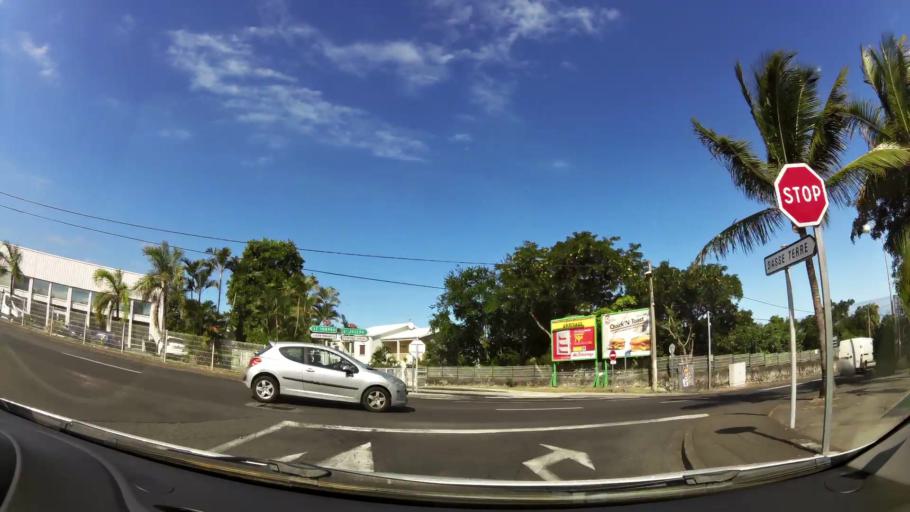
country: RE
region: Reunion
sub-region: Reunion
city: Saint-Pierre
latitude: -21.3303
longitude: 55.4794
